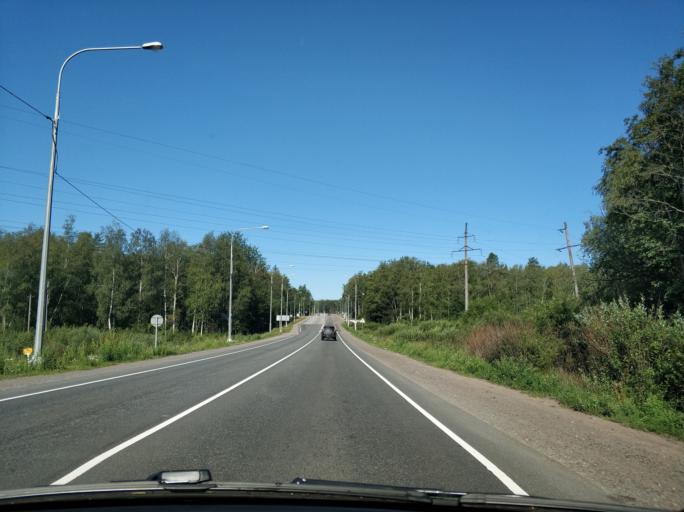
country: RU
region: Leningrad
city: Sapernoye
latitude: 60.6825
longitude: 29.9959
